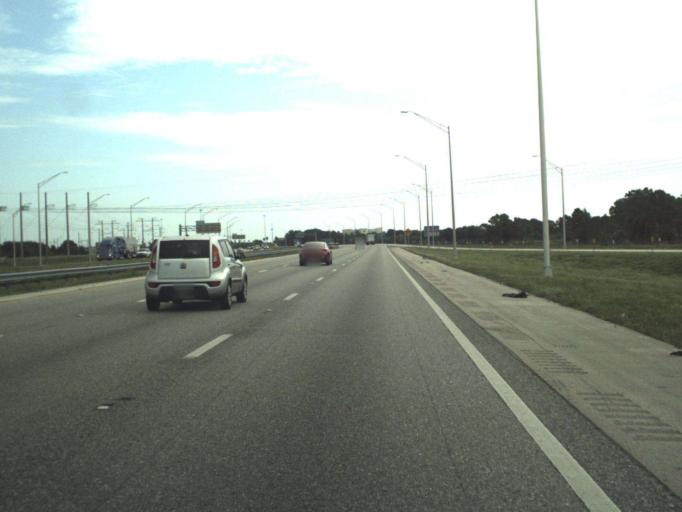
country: US
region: Florida
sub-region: Saint Lucie County
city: Port Saint Lucie
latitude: 27.2958
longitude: -80.4166
